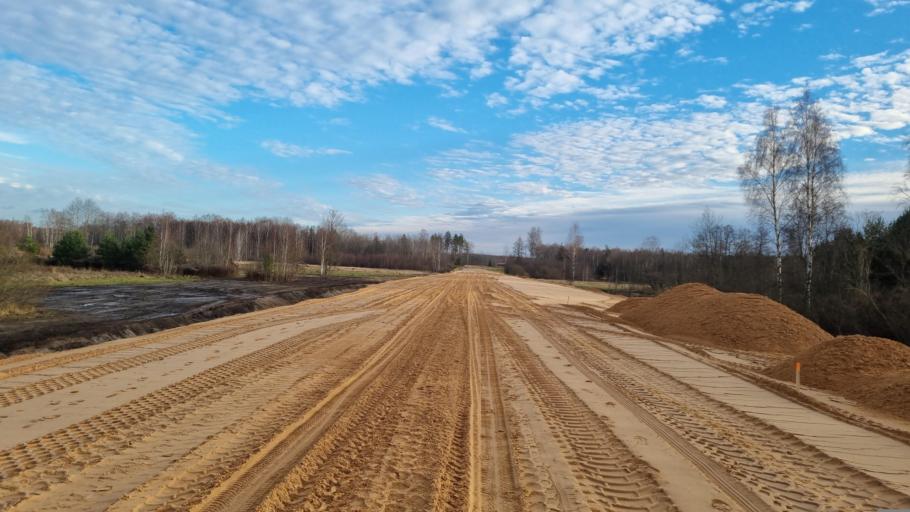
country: LV
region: Kekava
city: Kekava
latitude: 56.7847
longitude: 24.2284
